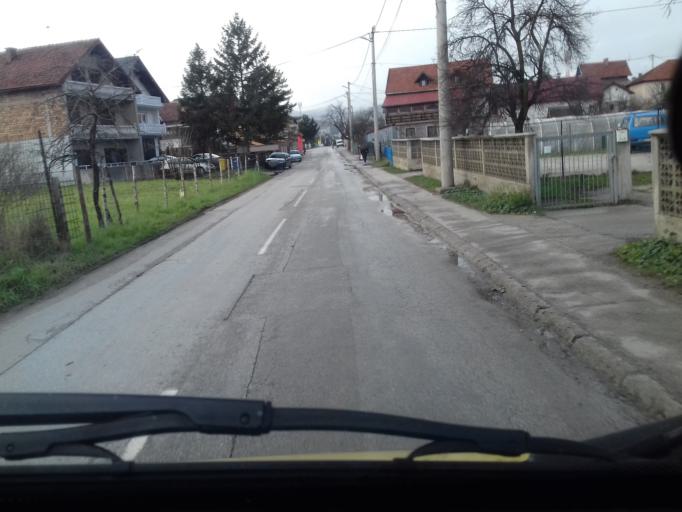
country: BA
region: Federation of Bosnia and Herzegovina
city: Zenica
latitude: 44.1914
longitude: 17.9406
